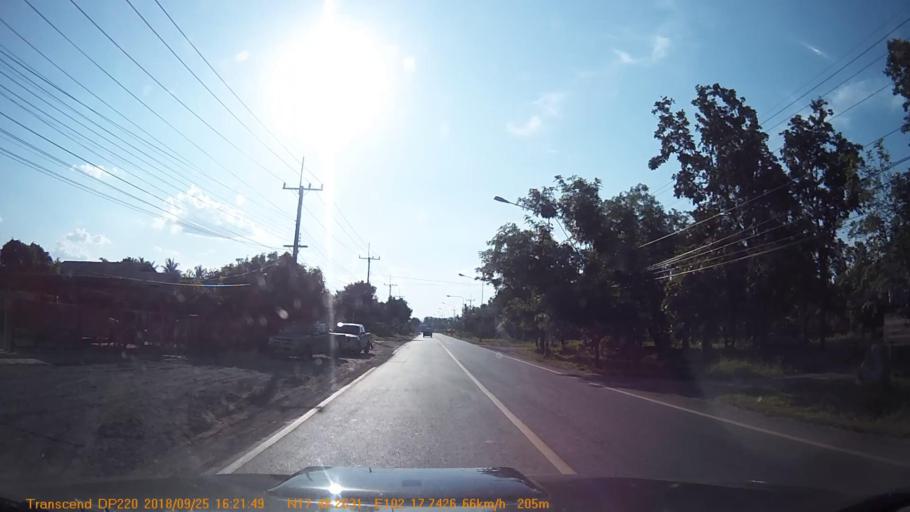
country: TH
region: Changwat Udon Thani
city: Nam Som
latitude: 17.8044
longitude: 102.2956
